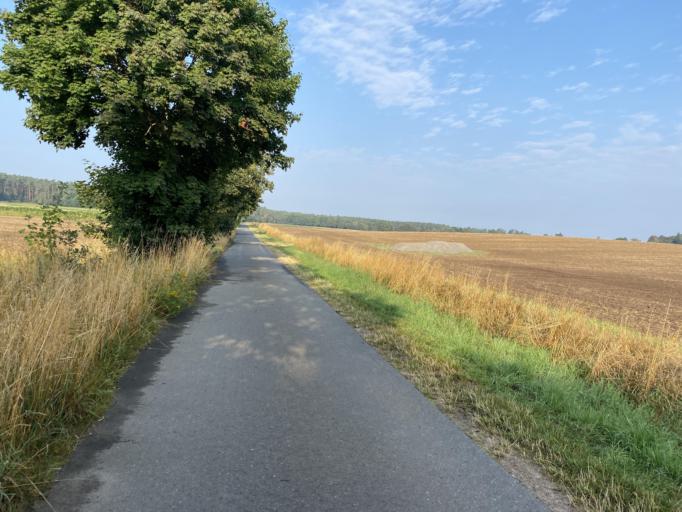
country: DE
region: Lower Saxony
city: Dahlenburg
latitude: 53.1637
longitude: 10.7066
